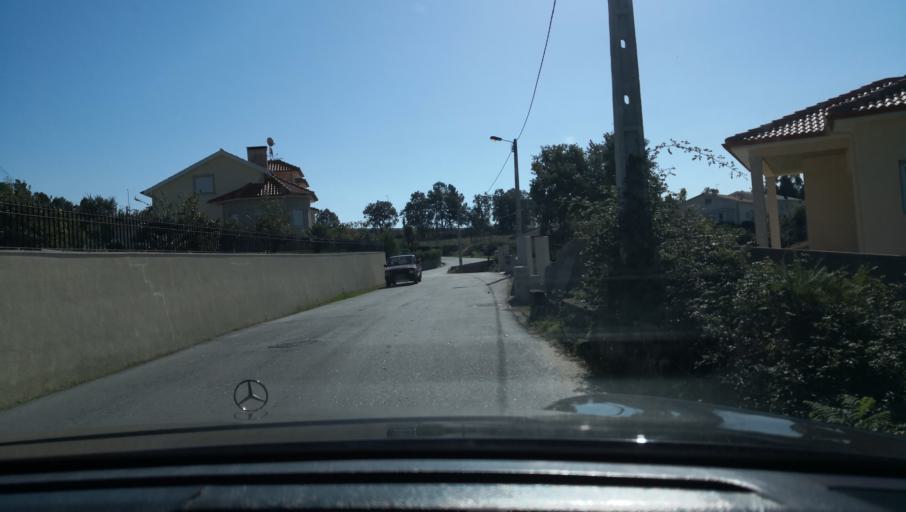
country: PT
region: Vila Real
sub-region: Vila Real
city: Vila Real
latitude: 41.3177
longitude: -7.6642
